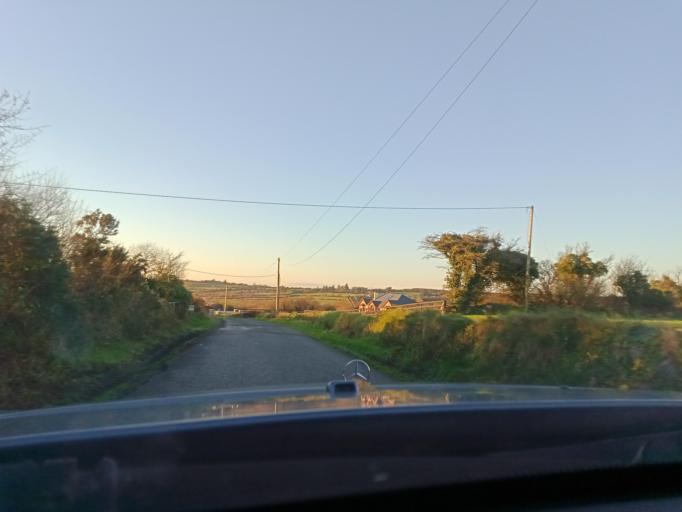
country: IE
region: Munster
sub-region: Waterford
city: Waterford
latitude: 52.3666
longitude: -7.1170
